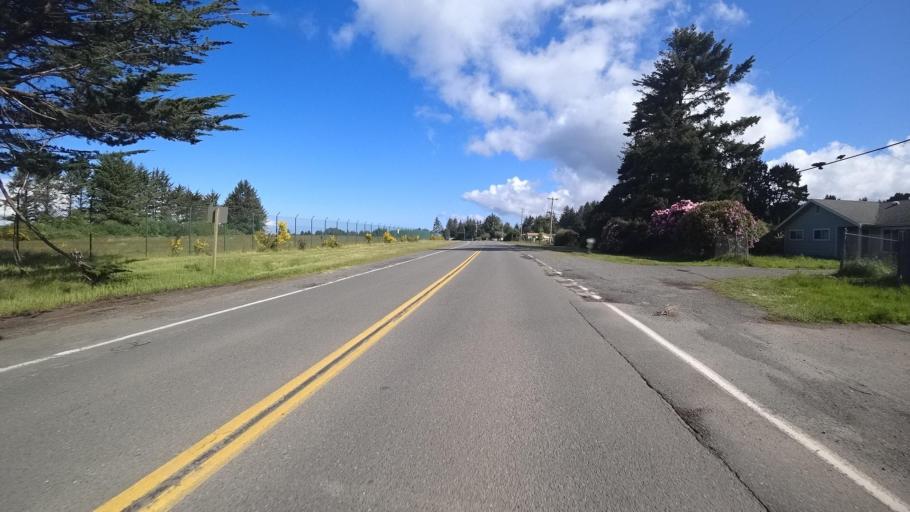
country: US
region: California
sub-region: Humboldt County
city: McKinleyville
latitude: 40.9784
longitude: -124.1007
